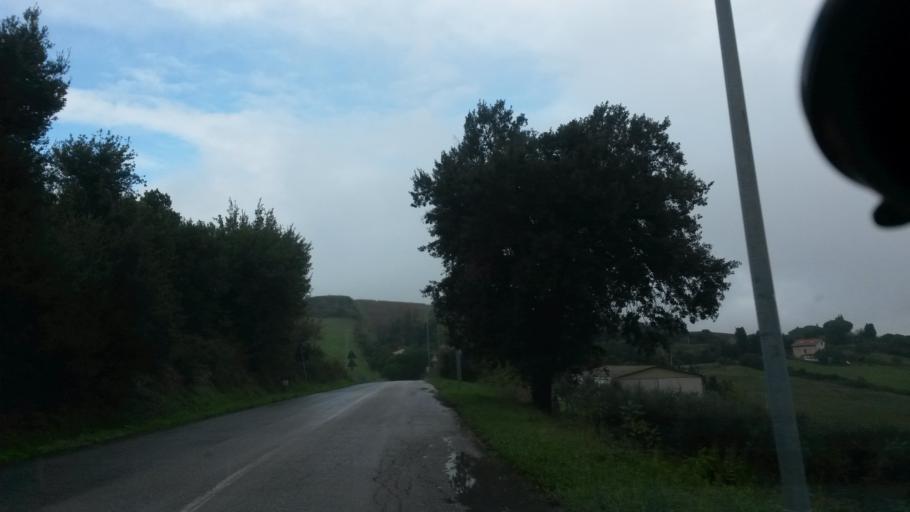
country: IT
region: Tuscany
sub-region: Provincia di Livorno
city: Rosignano Marittimo
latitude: 43.4182
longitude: 10.4598
